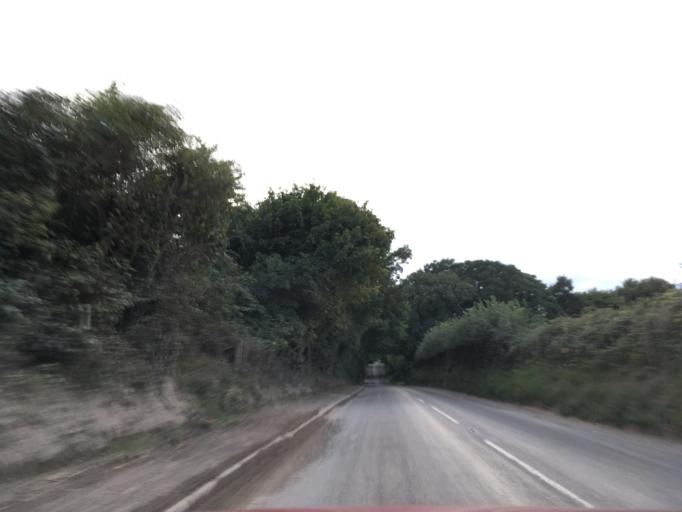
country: GB
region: England
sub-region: Wiltshire
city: Devizes
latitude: 51.3393
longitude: -1.9676
